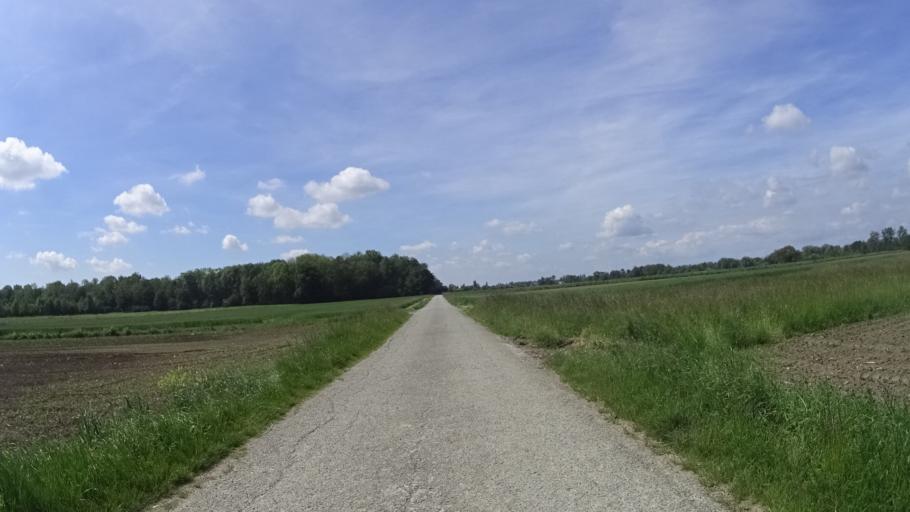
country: DE
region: Baden-Wuerttemberg
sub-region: Freiburg Region
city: Meissenheim
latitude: 48.4265
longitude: 7.7870
